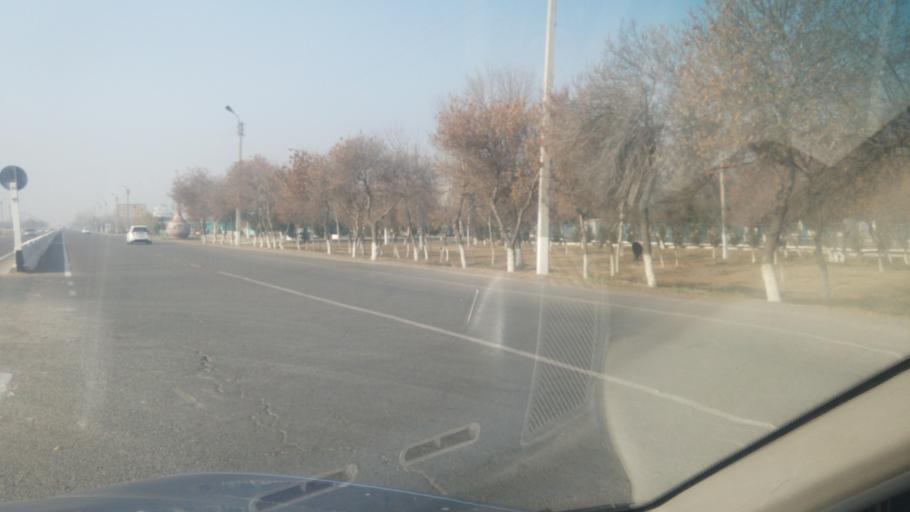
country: UZ
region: Sirdaryo
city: Guliston
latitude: 40.4887
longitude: 68.7484
